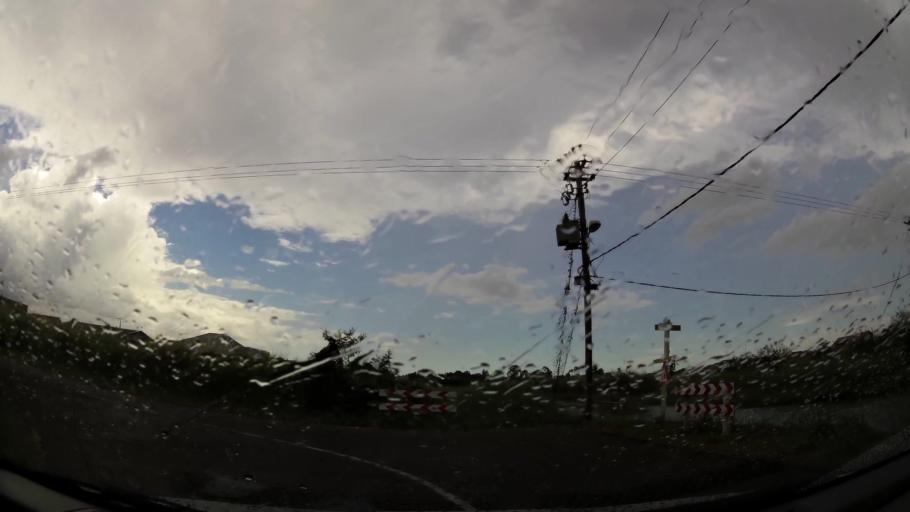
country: SR
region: Commewijne
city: Nieuw Amsterdam
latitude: 5.8568
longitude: -55.1179
